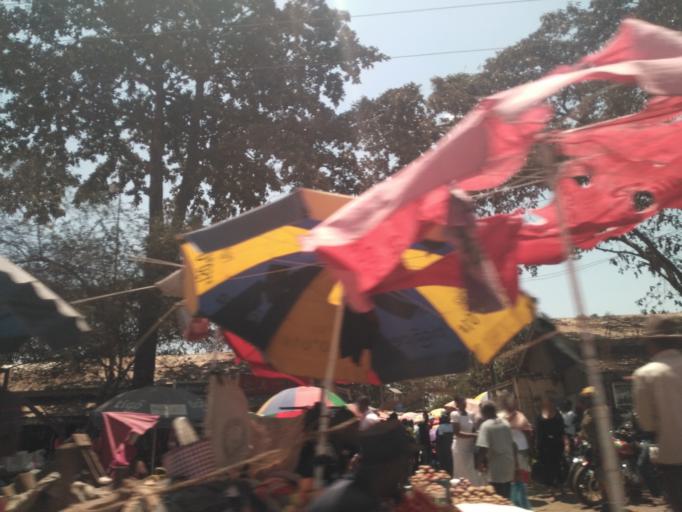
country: TZ
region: Arusha
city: Arusha
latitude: -3.3733
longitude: 36.6793
